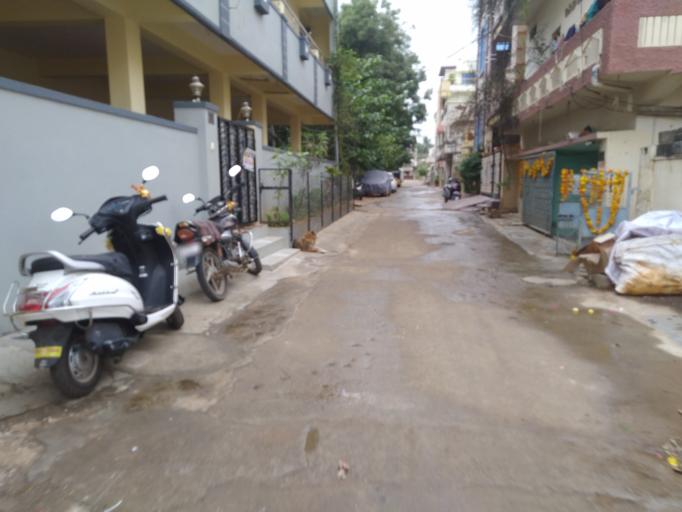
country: IN
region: Telangana
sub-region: Medak
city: Serilingampalle
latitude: 17.5036
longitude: 78.2884
